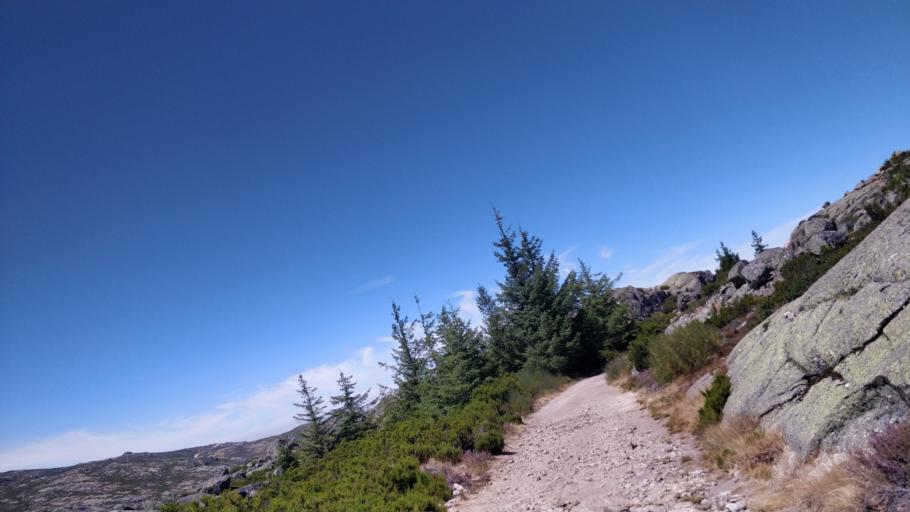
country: PT
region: Guarda
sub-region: Seia
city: Seia
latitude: 40.3638
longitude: -7.6315
